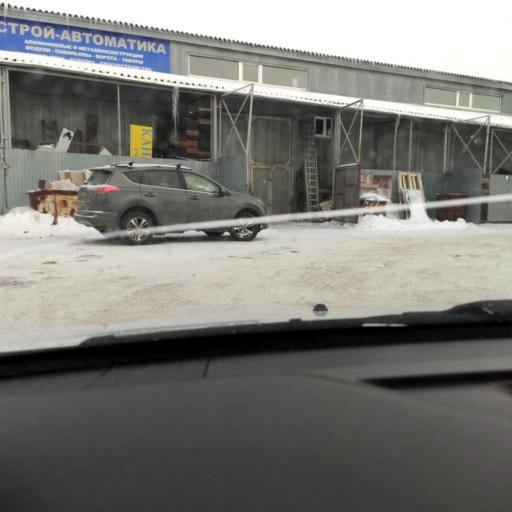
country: RU
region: Samara
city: Samara
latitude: 53.1968
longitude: 50.2642
